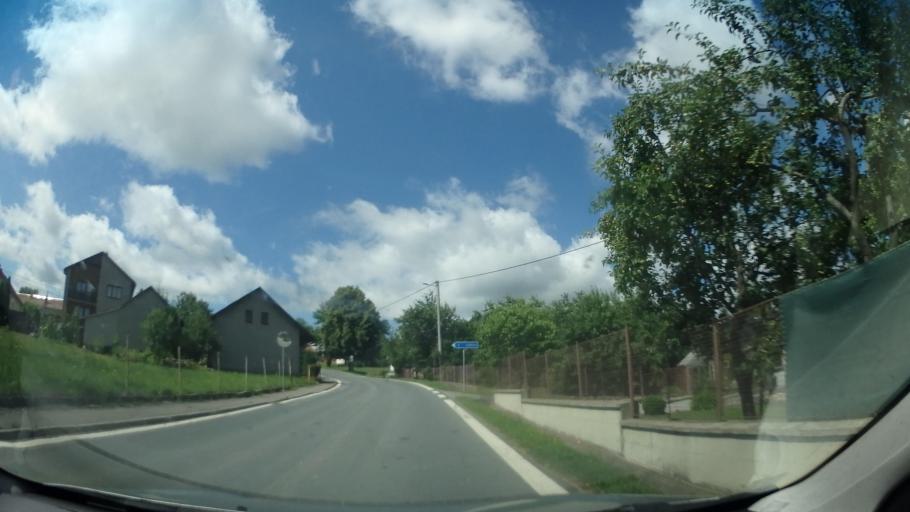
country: CZ
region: Vysocina
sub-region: Okres Zd'ar nad Sazavou
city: Zd'ar nad Sazavou
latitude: 49.5828
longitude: 15.9672
